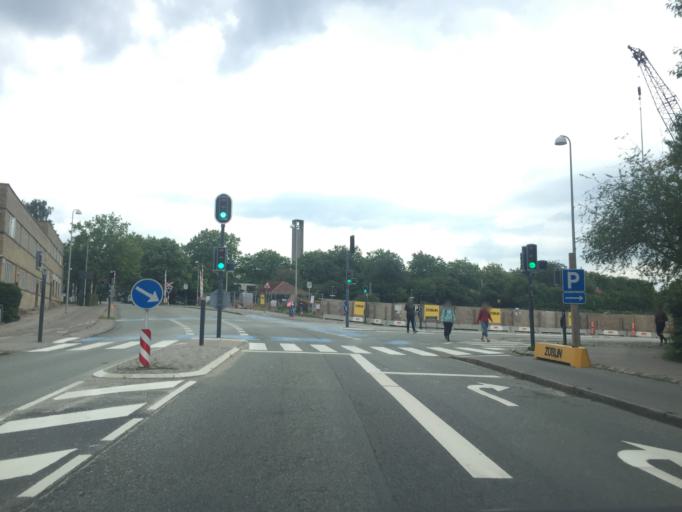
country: DK
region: Capital Region
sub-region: Lyngby-Tarbaek Kommune
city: Kongens Lyngby
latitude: 55.7730
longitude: 12.5050
